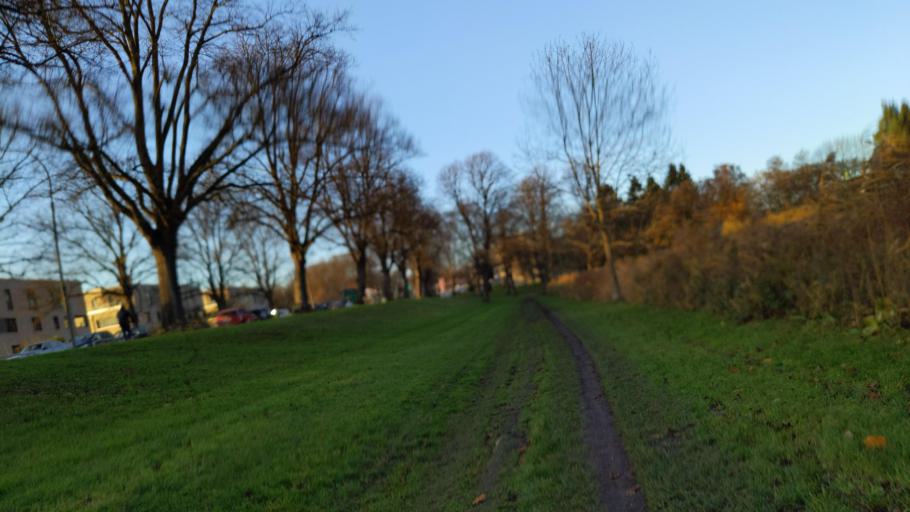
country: DE
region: Schleswig-Holstein
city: Luebeck
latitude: 53.8730
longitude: 10.6971
